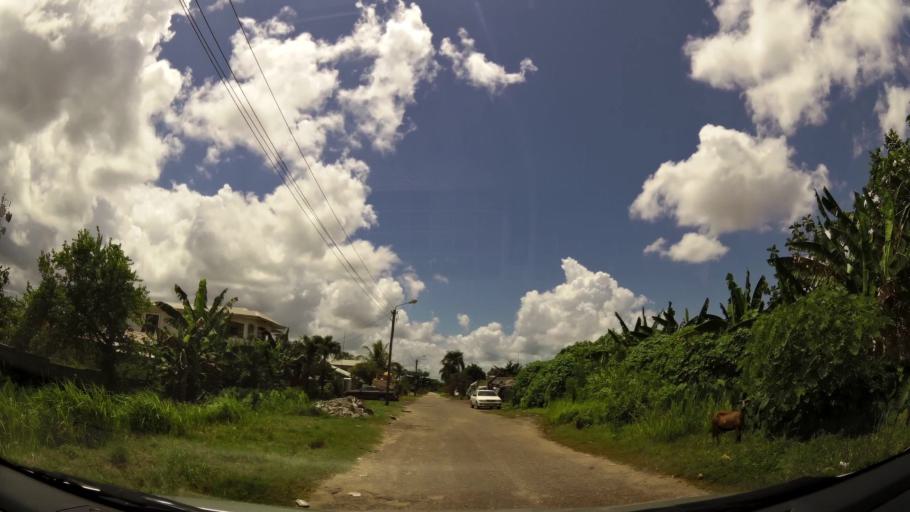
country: SR
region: Paramaribo
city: Paramaribo
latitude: 5.8606
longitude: -55.1663
